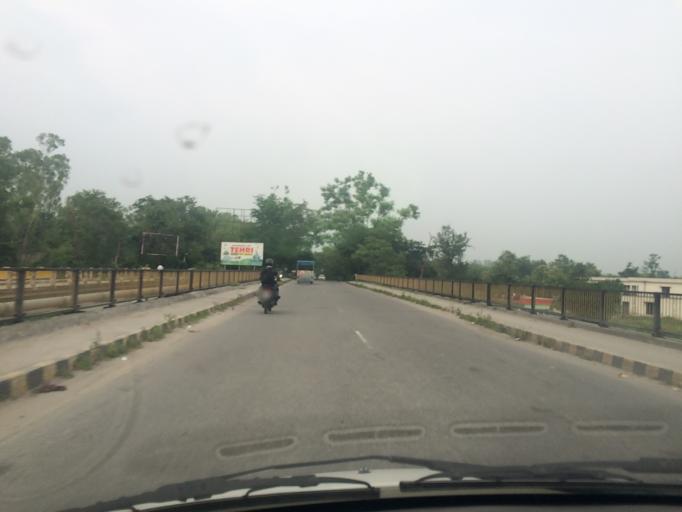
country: IN
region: Uttarakhand
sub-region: Dehradun
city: Doiwala
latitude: 30.1783
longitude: 78.1312
